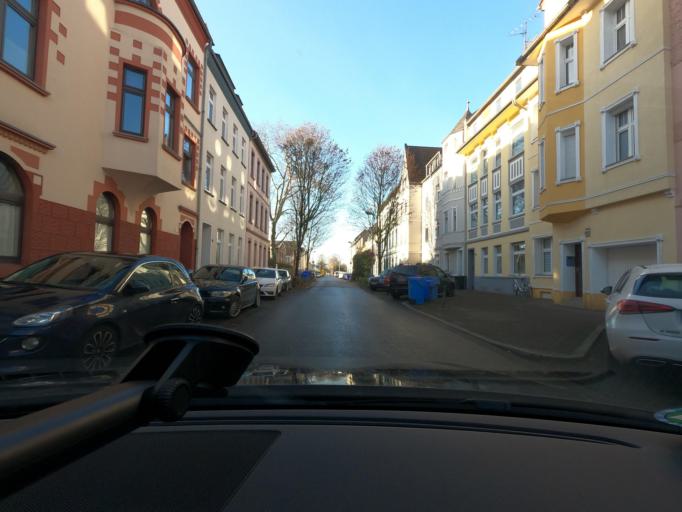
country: DE
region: North Rhine-Westphalia
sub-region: Regierungsbezirk Dusseldorf
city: Krefeld
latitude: 51.3311
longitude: 6.5449
